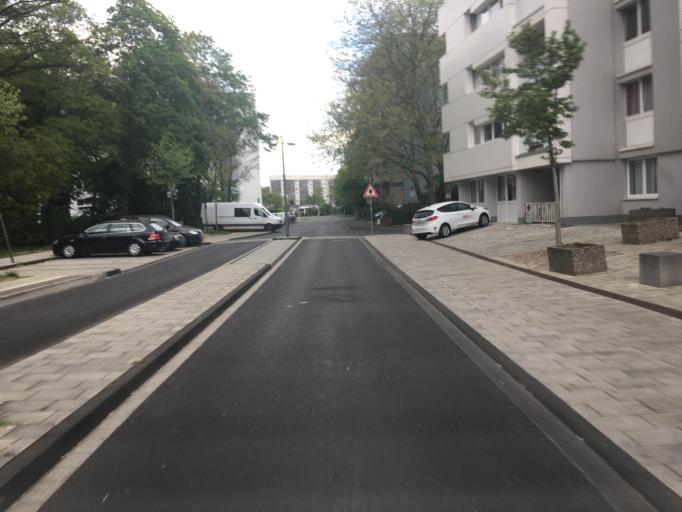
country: DE
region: North Rhine-Westphalia
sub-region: Regierungsbezirk Koln
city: Mengenich
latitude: 50.9801
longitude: 6.8653
